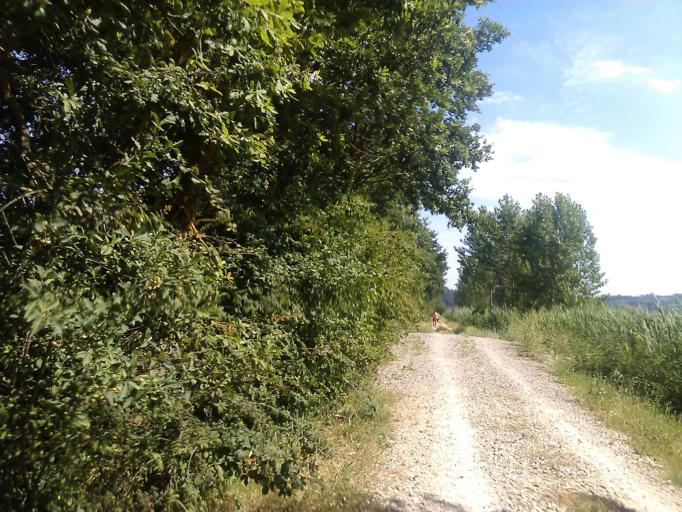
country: IT
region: Tuscany
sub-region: Provincia di Siena
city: Chiusi
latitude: 43.0610
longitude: 11.9333
